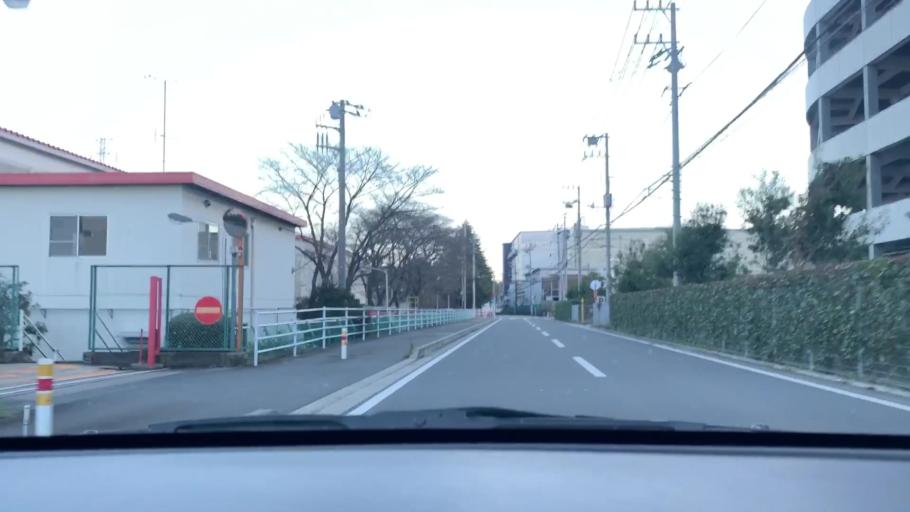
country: JP
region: Chiba
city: Kashiwa
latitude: 35.9081
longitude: 139.9464
